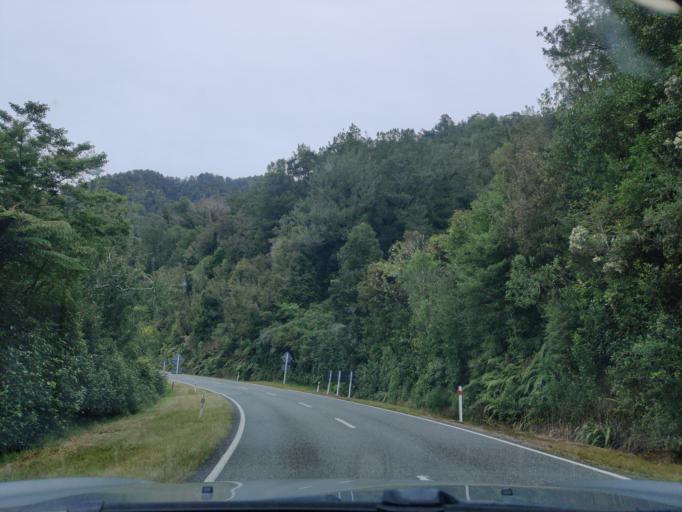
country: NZ
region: West Coast
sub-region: Buller District
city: Westport
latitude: -41.8499
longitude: 171.7421
